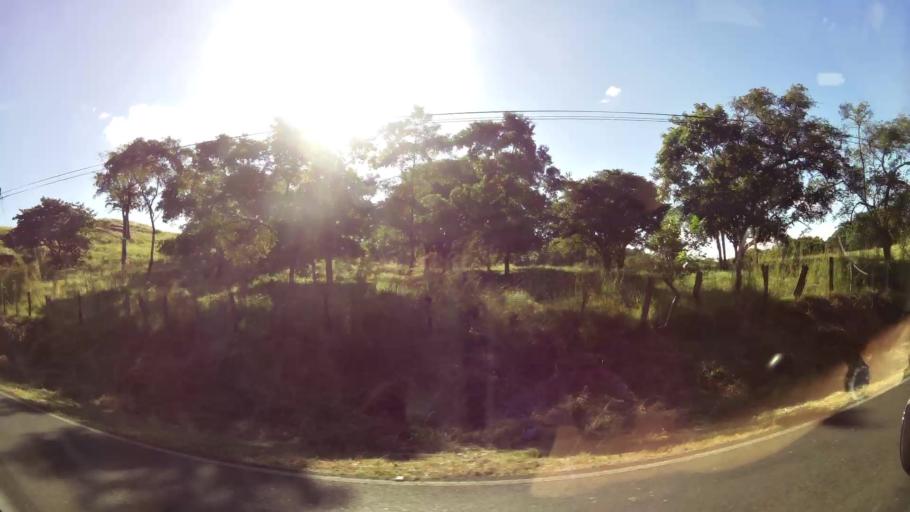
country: CR
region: Guanacaste
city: Belen
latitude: 10.3717
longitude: -85.6310
